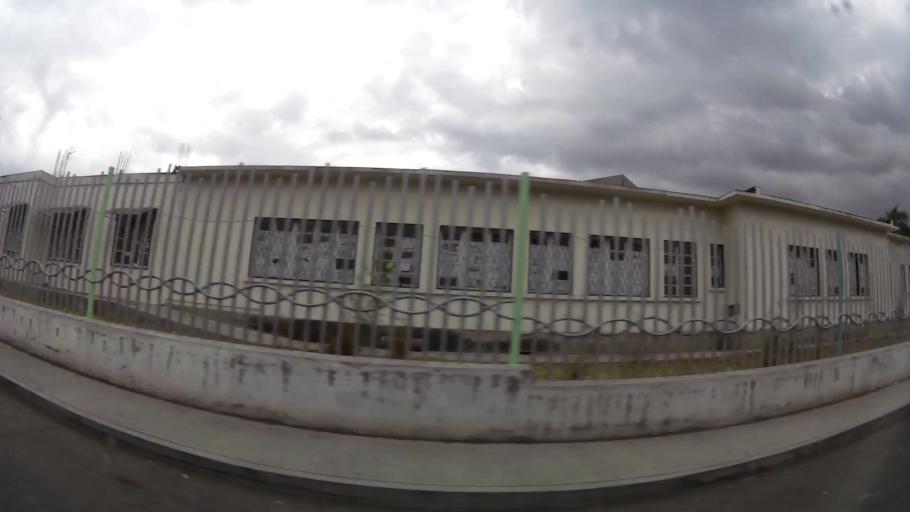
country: EC
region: Tungurahua
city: Ambato
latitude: -1.2316
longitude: -78.6220
